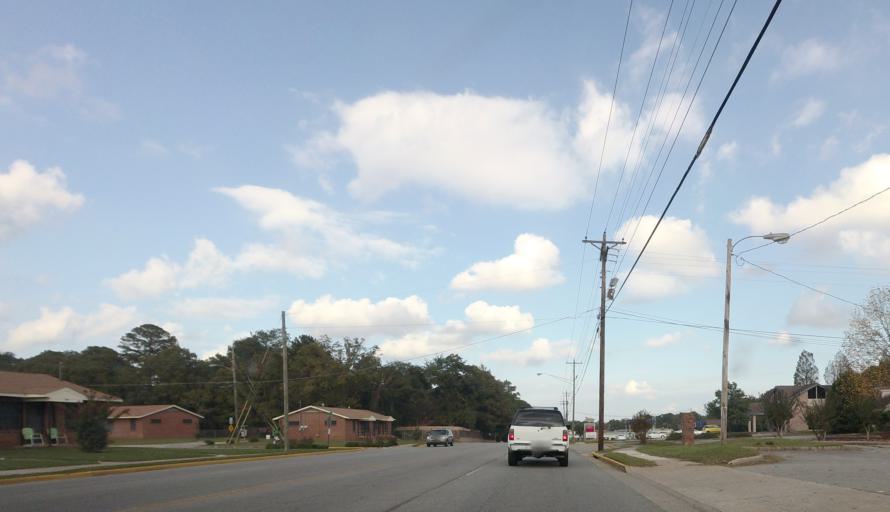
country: US
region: Georgia
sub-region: Houston County
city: Warner Robins
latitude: 32.6281
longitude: -83.6169
